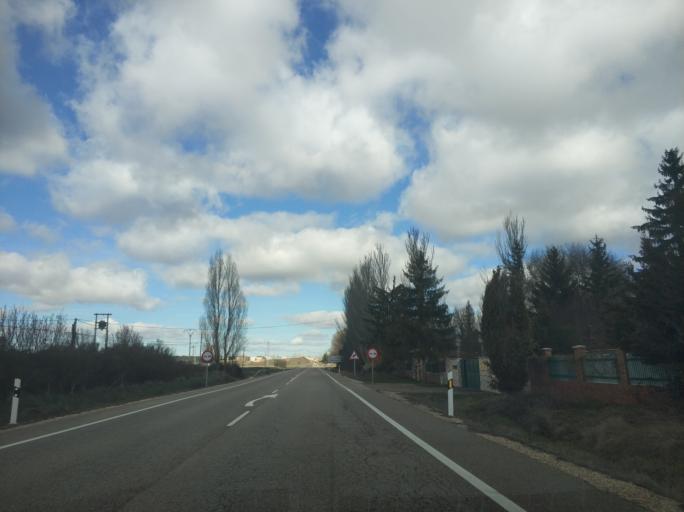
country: ES
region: Castille and Leon
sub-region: Provincia de Burgos
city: Revillarruz
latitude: 42.2323
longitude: -3.6642
